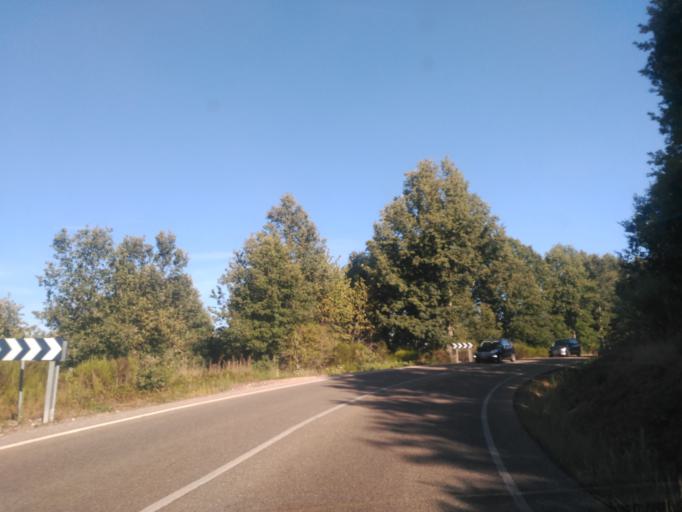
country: ES
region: Castille and Leon
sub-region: Provincia de Zamora
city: Galende
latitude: 42.1011
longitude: -6.6528
